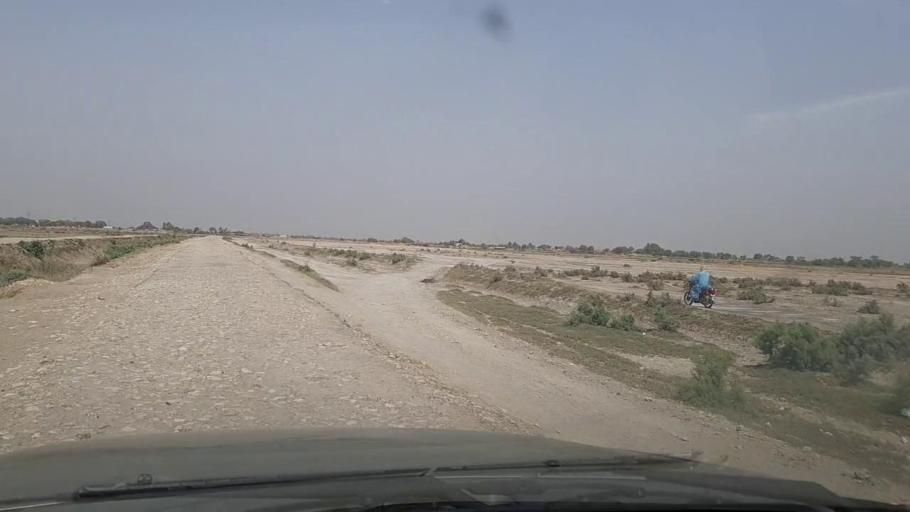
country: PK
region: Balochistan
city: Sohbatpur
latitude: 28.4122
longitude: 68.6948
